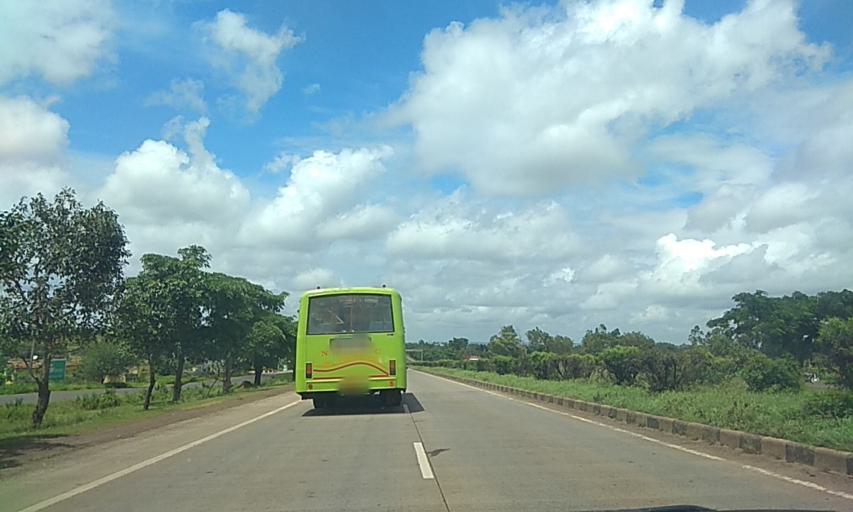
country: IN
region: Karnataka
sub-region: Belgaum
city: Sankeshwar
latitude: 16.1532
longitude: 74.5177
